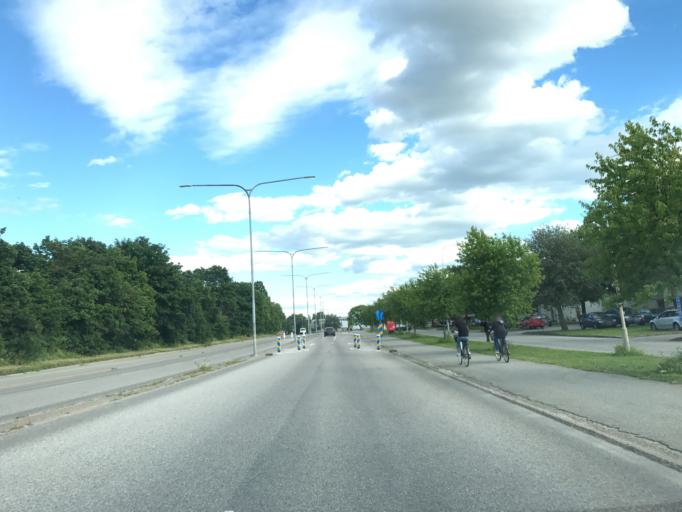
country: SE
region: OErebro
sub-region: Orebro Kommun
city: Orebro
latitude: 59.2834
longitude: 15.1892
